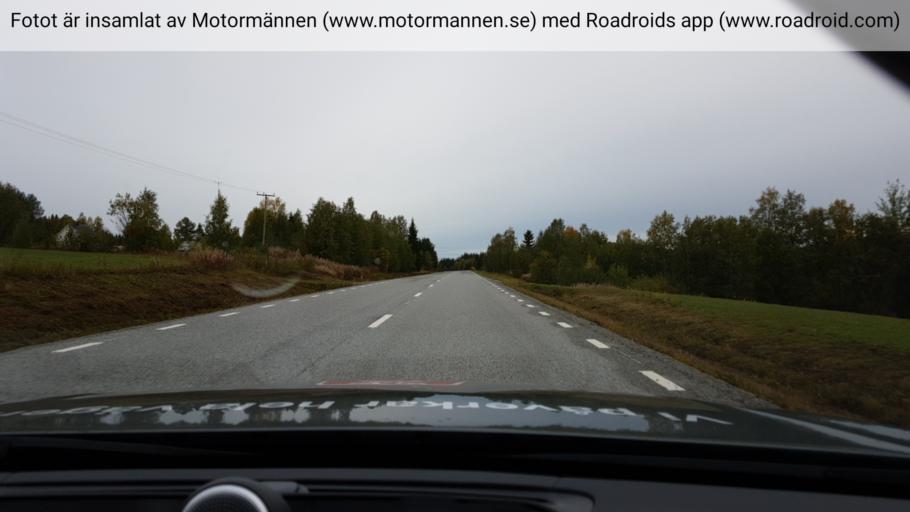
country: SE
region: Jaemtland
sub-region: Stroemsunds Kommun
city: Stroemsund
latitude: 64.2169
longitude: 15.5553
